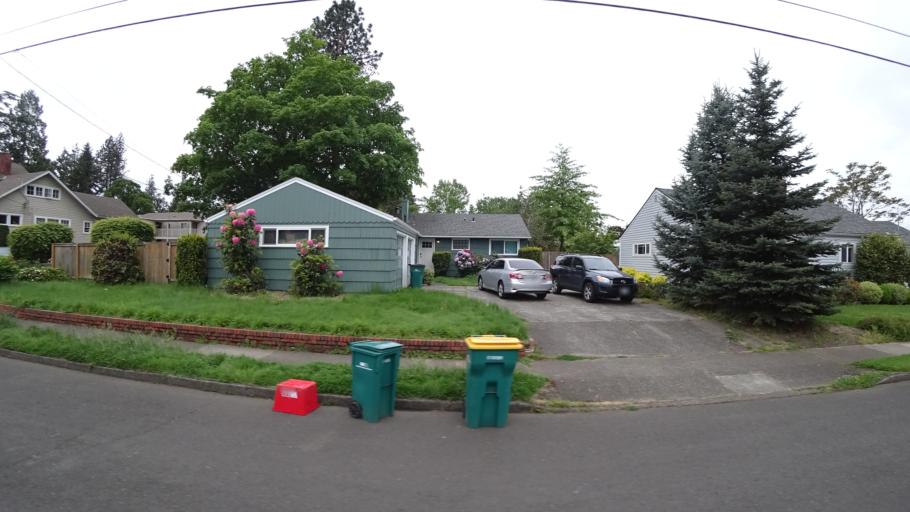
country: US
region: Oregon
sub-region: Washington County
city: Beaverton
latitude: 45.4801
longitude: -122.8019
